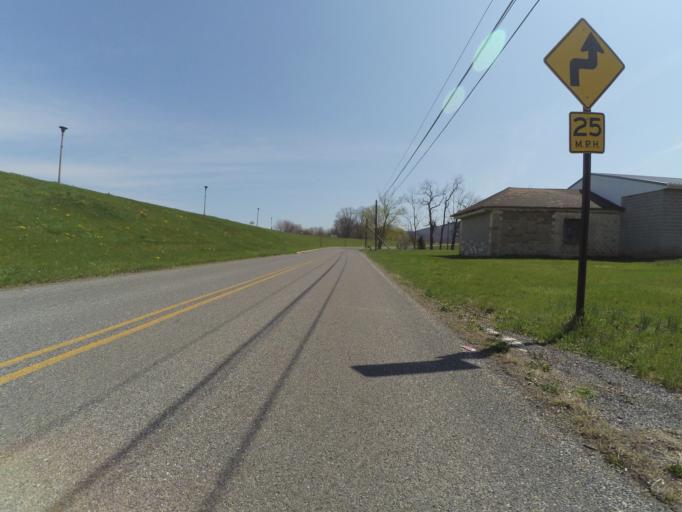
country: US
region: Pennsylvania
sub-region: Clinton County
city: Dunnstown
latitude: 41.1385
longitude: -77.4208
